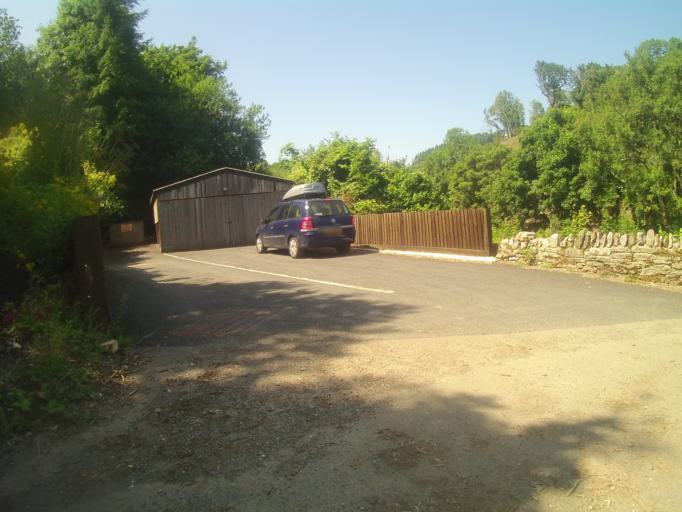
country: GB
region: England
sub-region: Devon
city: Dartmouth
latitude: 50.3559
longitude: -3.6018
